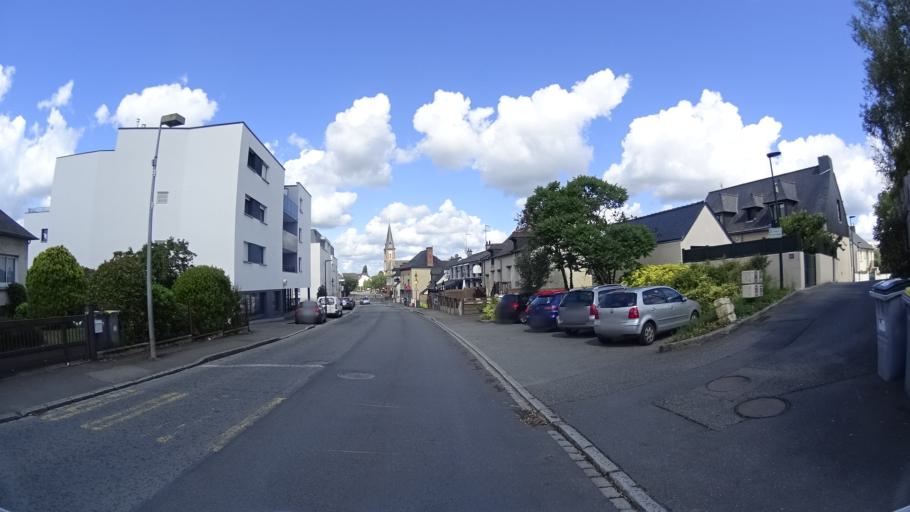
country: FR
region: Brittany
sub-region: Departement d'Ille-et-Vilaine
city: Chartres-de-Bretagne
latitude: 48.0419
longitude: -1.7040
